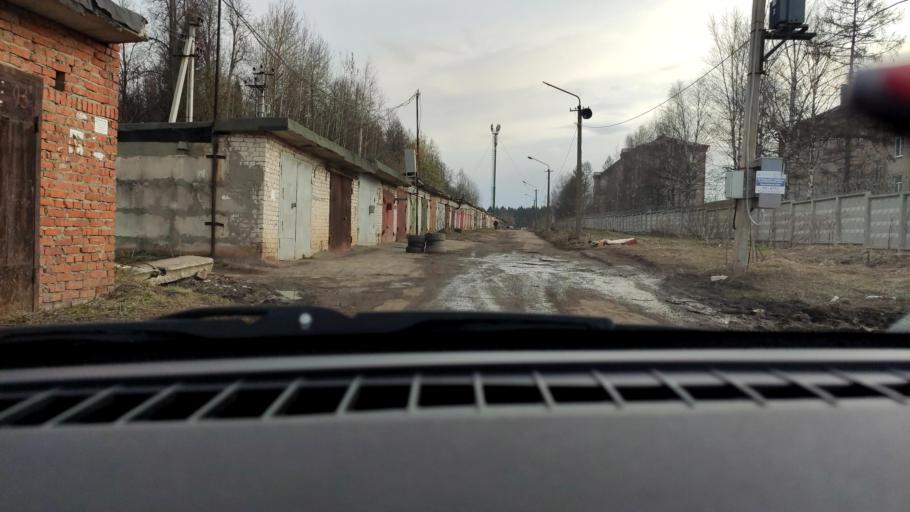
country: RU
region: Perm
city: Froly
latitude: 57.9712
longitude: 56.3206
